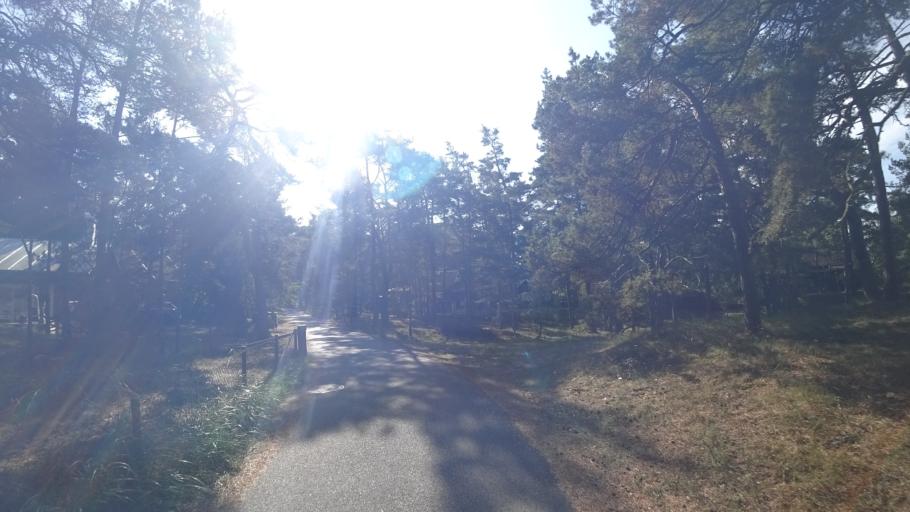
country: SE
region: Skane
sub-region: Kristianstads Kommun
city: Ahus
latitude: 55.9159
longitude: 14.3083
